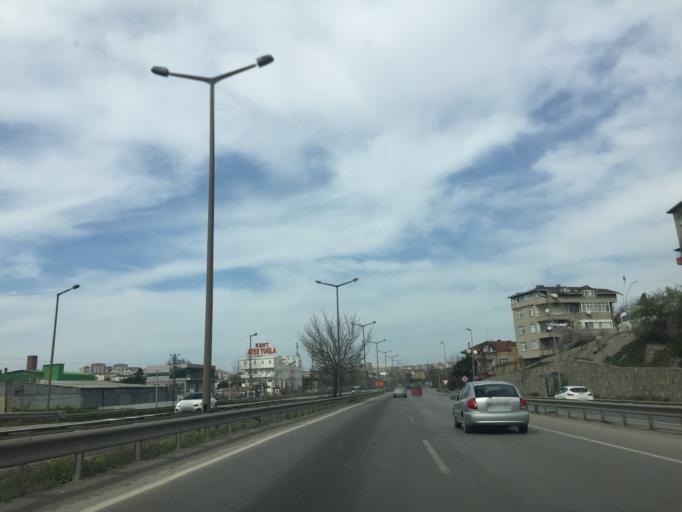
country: TR
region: Kocaeli
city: Darica
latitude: 40.8183
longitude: 29.3651
